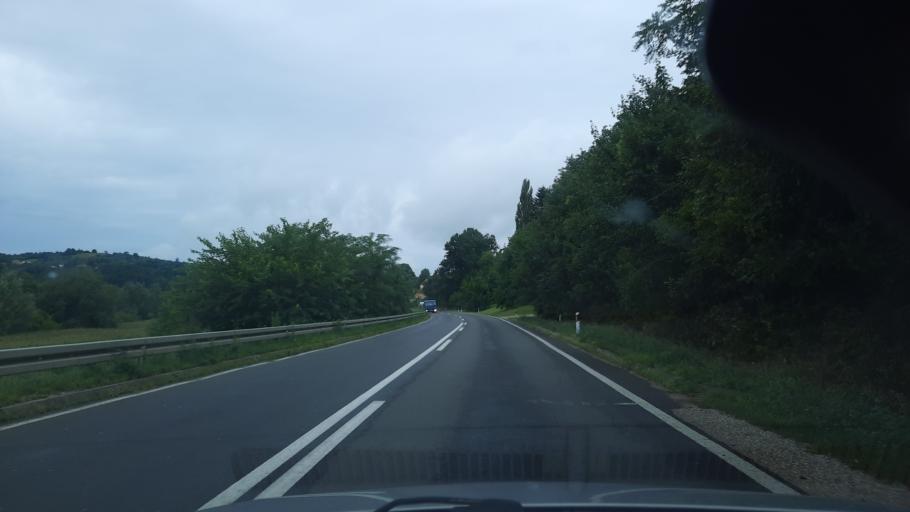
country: RS
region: Central Serbia
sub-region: Sumadijski Okrug
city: Knic
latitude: 43.9704
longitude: 20.8114
